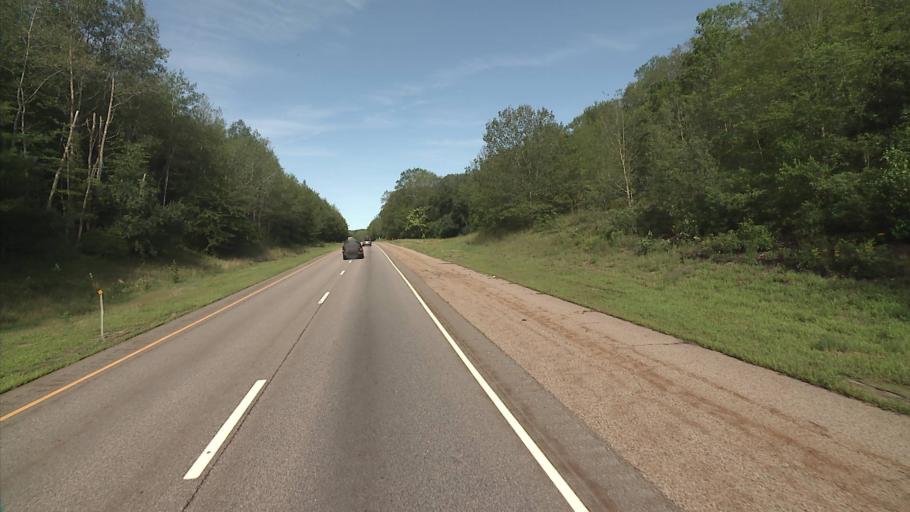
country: US
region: Connecticut
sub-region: New London County
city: Colchester
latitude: 41.5681
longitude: -72.2614
